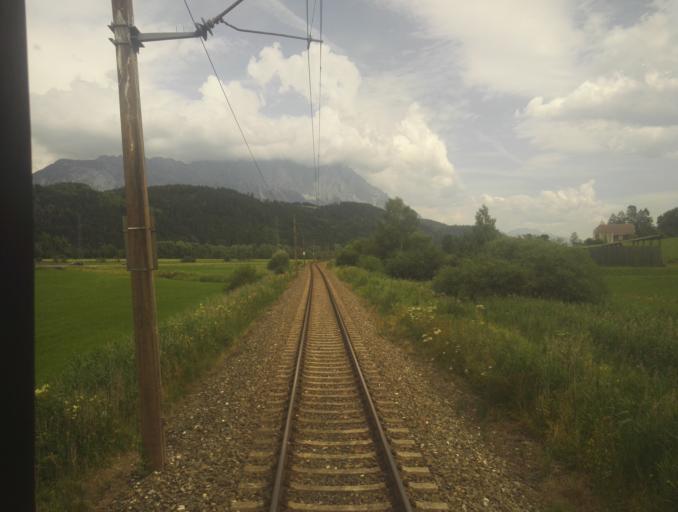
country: AT
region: Styria
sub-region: Politischer Bezirk Liezen
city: Grosssolk
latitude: 47.4454
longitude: 13.9558
